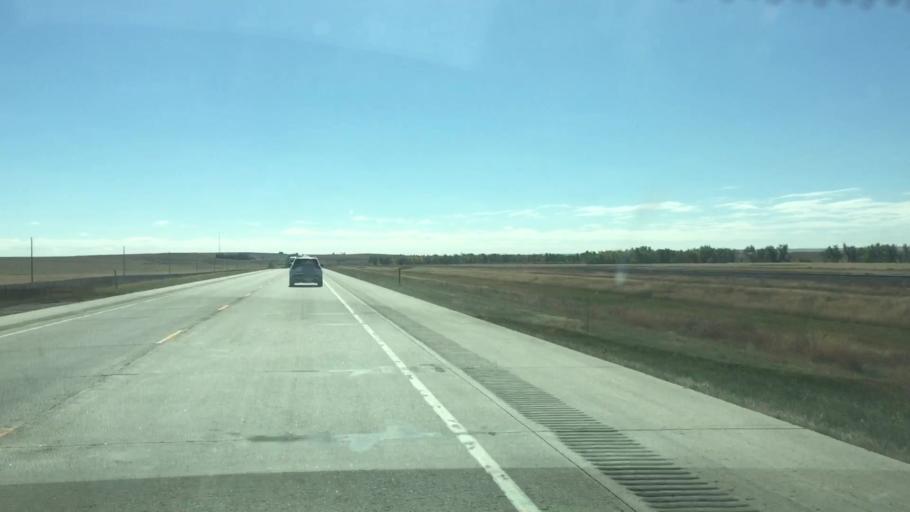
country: US
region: Colorado
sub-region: Lincoln County
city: Limon
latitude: 39.2293
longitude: -103.6150
